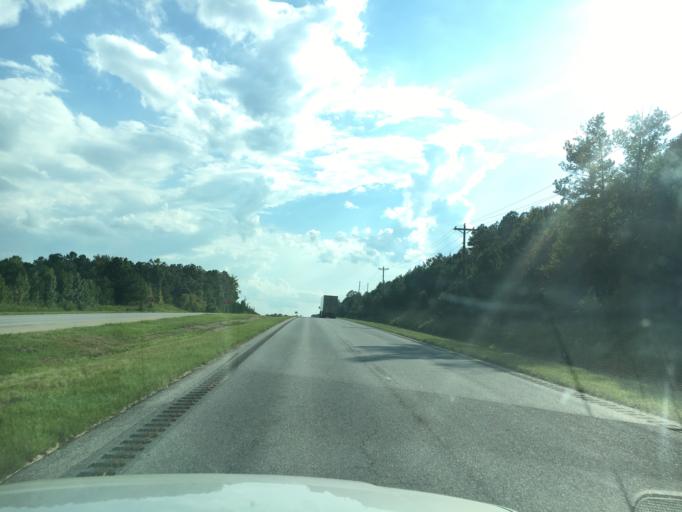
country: US
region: South Carolina
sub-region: Greenwood County
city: Ninety Six
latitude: 34.2971
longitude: -82.0103
